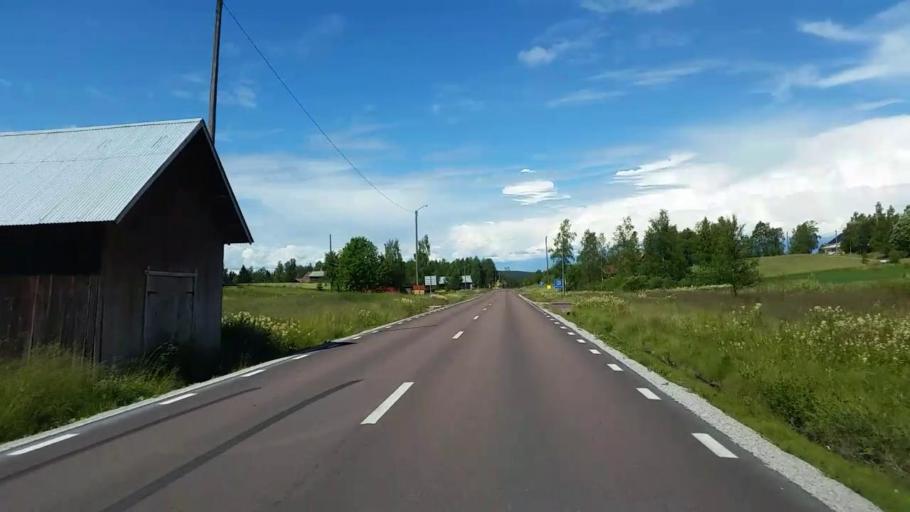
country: SE
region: Dalarna
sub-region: Rattviks Kommun
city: Raettvik
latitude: 61.0385
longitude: 15.1987
